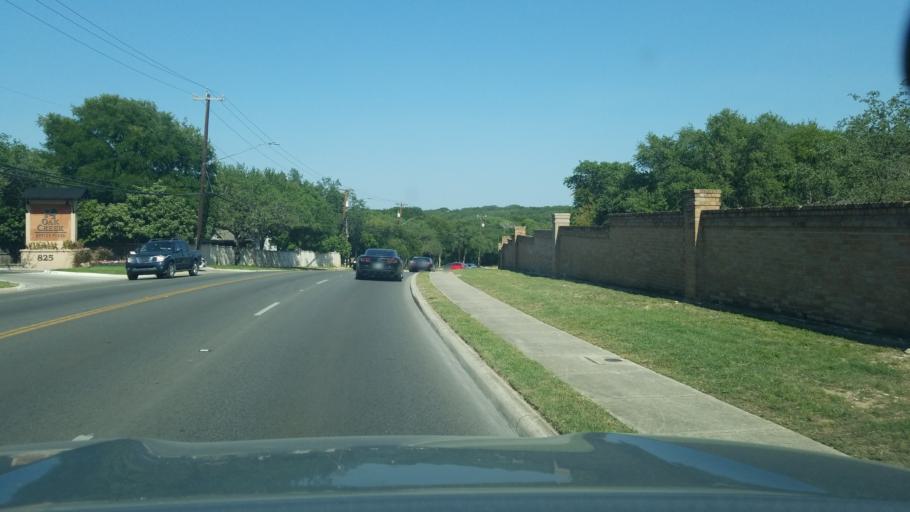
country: US
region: Texas
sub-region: Bexar County
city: Hollywood Park
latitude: 29.5814
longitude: -98.5046
